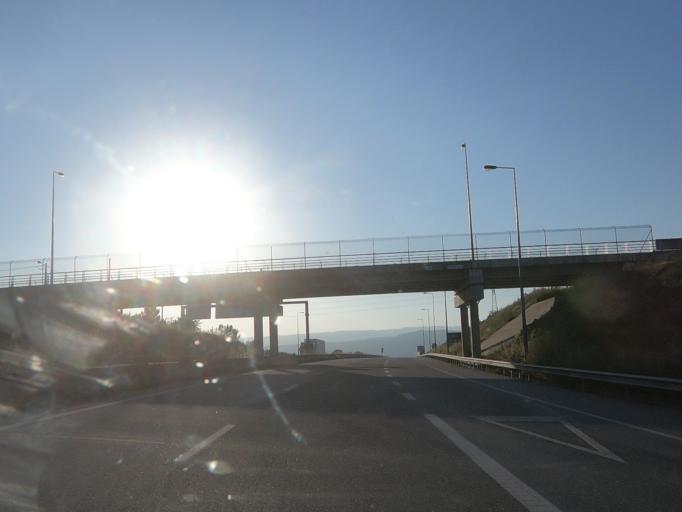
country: PT
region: Guarda
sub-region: Celorico da Beira
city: Celorico da Beira
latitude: 40.6248
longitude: -7.4016
